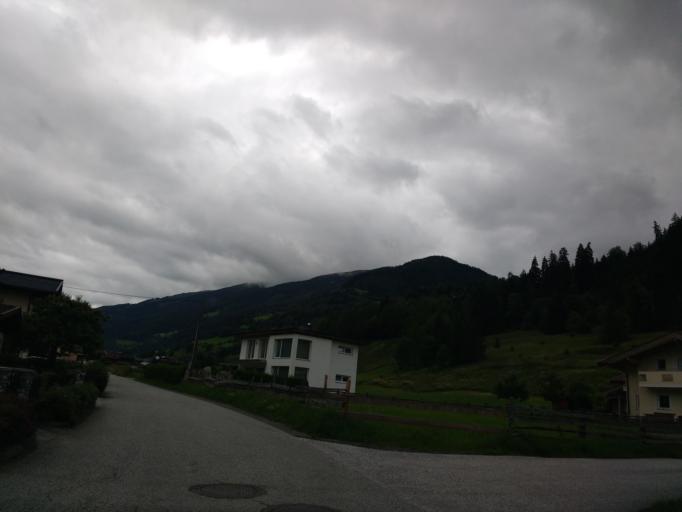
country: AT
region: Salzburg
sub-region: Politischer Bezirk Zell am See
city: Hollersbach im Pinzgau
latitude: 47.2808
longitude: 12.3854
